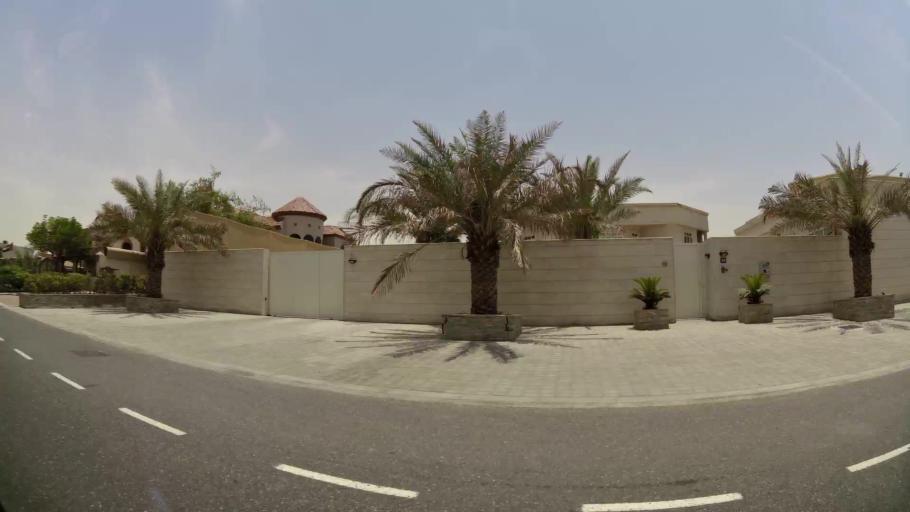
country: AE
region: Ash Shariqah
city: Sharjah
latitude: 25.2090
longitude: 55.3894
